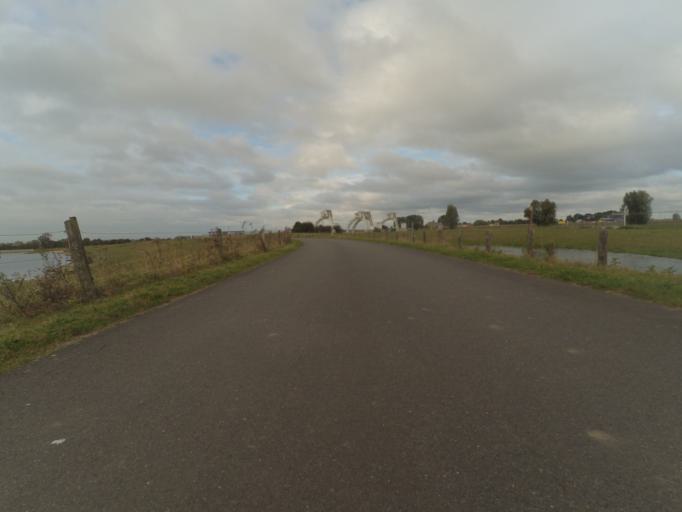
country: NL
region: Utrecht
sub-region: Gemeente Utrechtse Heuvelrug
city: Leersum
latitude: 51.9728
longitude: 5.4120
